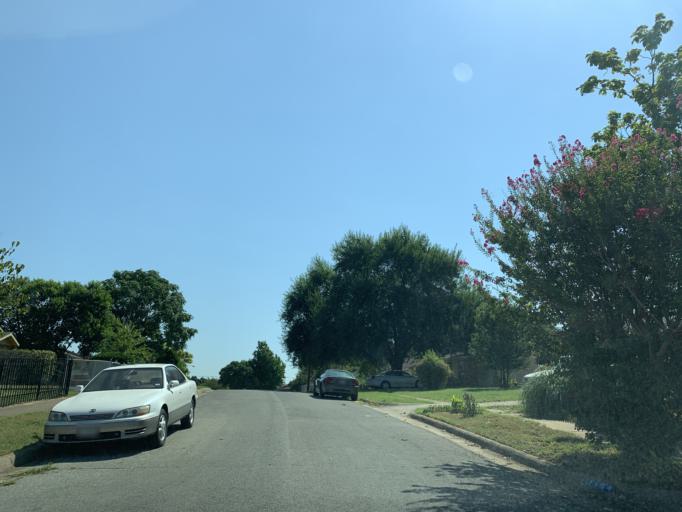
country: US
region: Texas
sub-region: Dallas County
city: Hutchins
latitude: 32.6685
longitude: -96.7473
